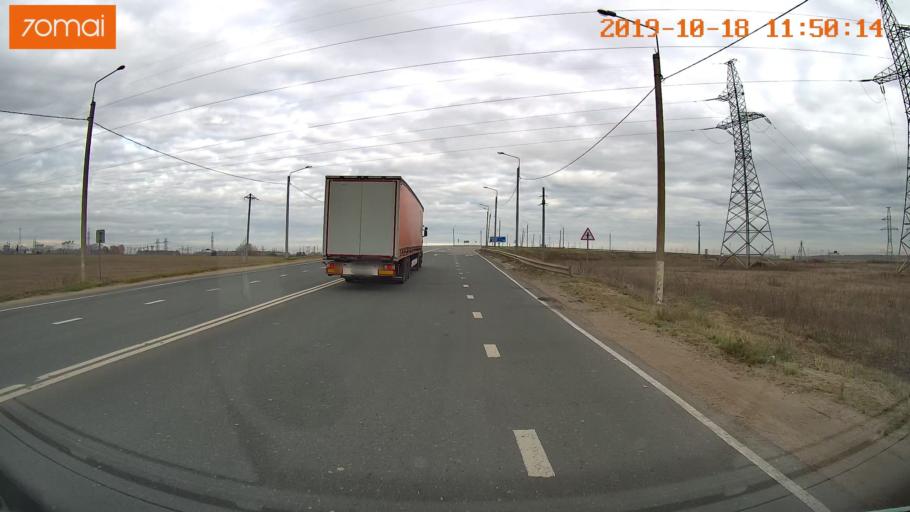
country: RU
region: Rjazan
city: Mikhaylov
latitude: 54.2594
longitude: 39.0018
